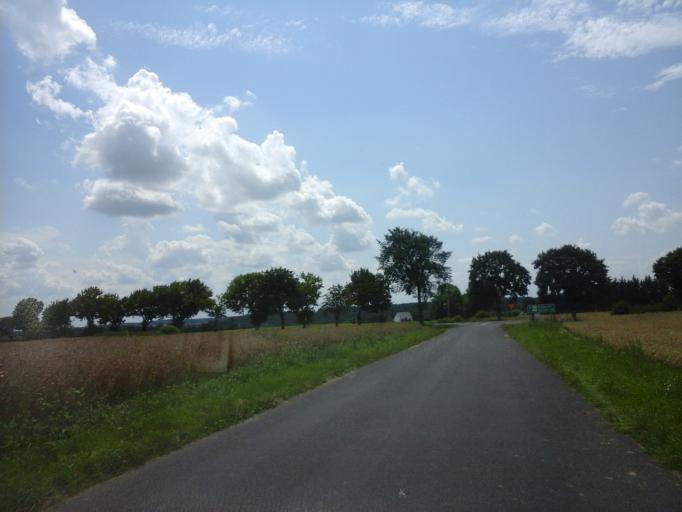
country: PL
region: West Pomeranian Voivodeship
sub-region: Powiat choszczenski
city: Recz
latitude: 53.2705
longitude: 15.4959
